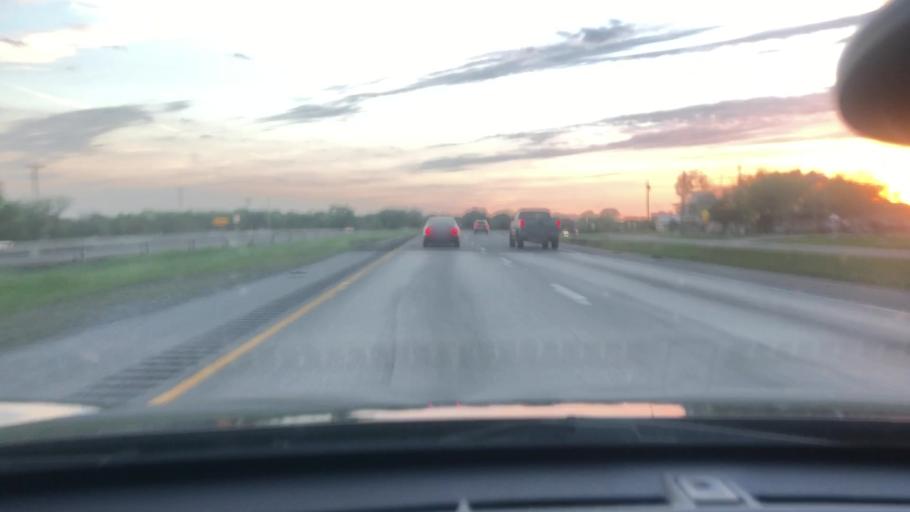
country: US
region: Texas
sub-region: Jackson County
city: Edna
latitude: 28.9616
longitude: -96.6800
